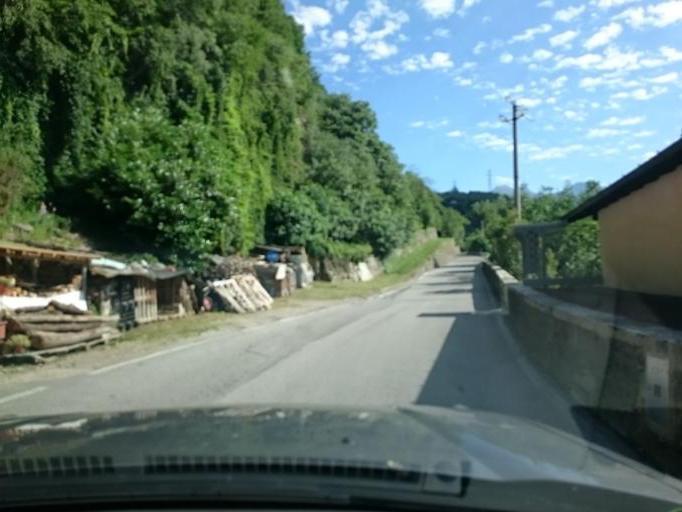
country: IT
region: Lombardy
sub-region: Provincia di Brescia
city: Capo di Ponte
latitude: 46.0301
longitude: 10.3345
